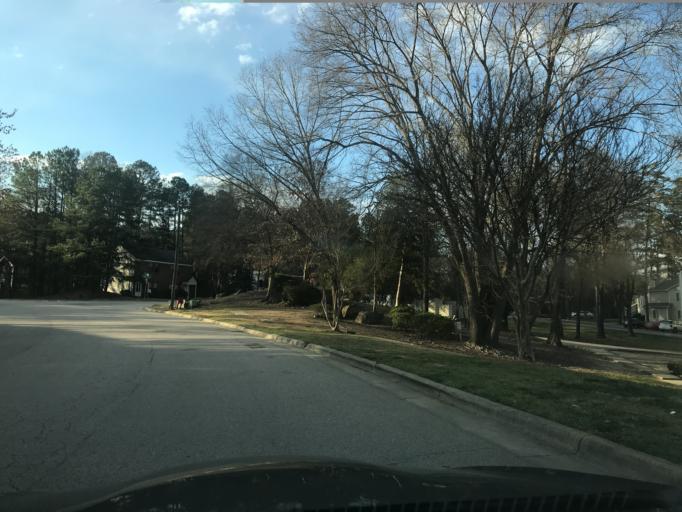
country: US
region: North Carolina
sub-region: Wake County
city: Raleigh
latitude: 35.8460
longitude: -78.5701
